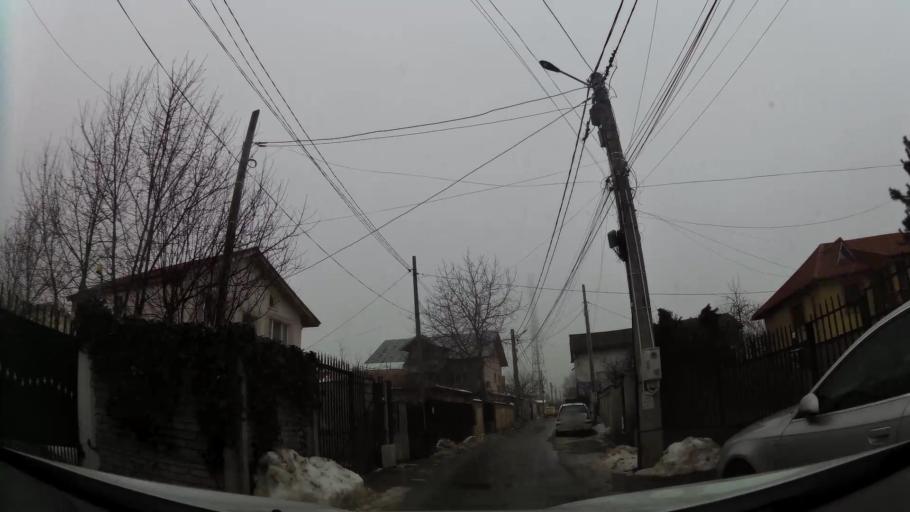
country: RO
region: Ilfov
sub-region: Comuna Chiajna
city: Rosu
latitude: 44.4469
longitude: 26.0117
